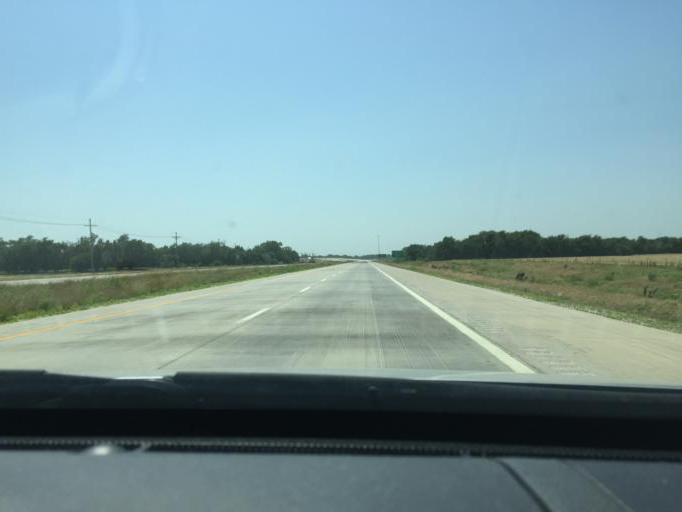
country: US
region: Kansas
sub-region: Reno County
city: South Hutchinson
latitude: 38.0290
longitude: -97.8897
